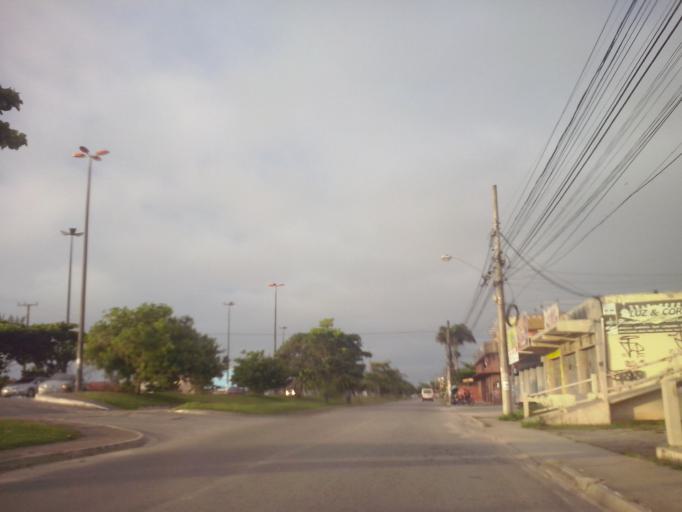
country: BR
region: Rio de Janeiro
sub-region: Rio Das Ostras
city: Rio das Ostras
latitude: -22.5444
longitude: -41.9720
